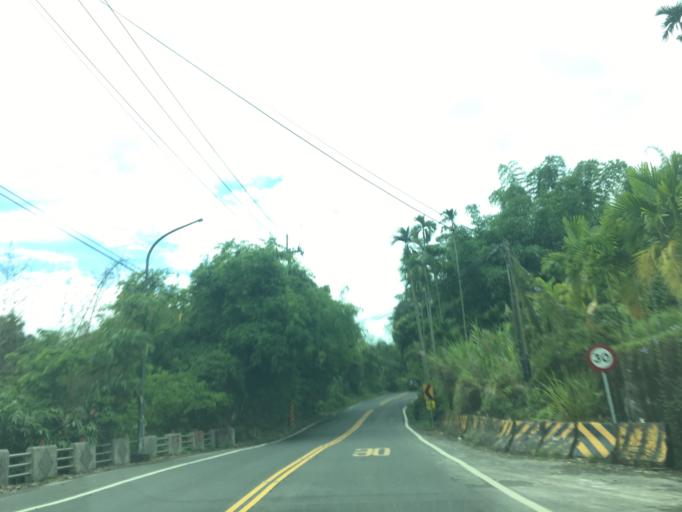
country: TW
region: Taiwan
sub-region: Yunlin
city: Douliu
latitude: 23.5729
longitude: 120.5649
